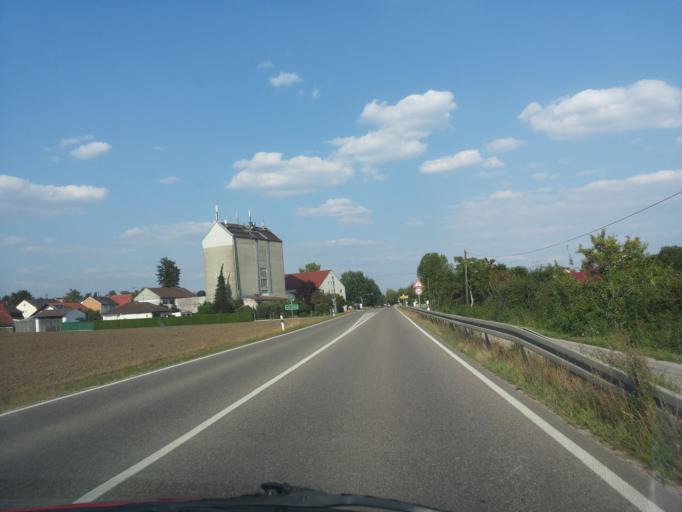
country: DE
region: Bavaria
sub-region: Upper Bavaria
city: Bergheim
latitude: 48.7632
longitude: 11.2732
